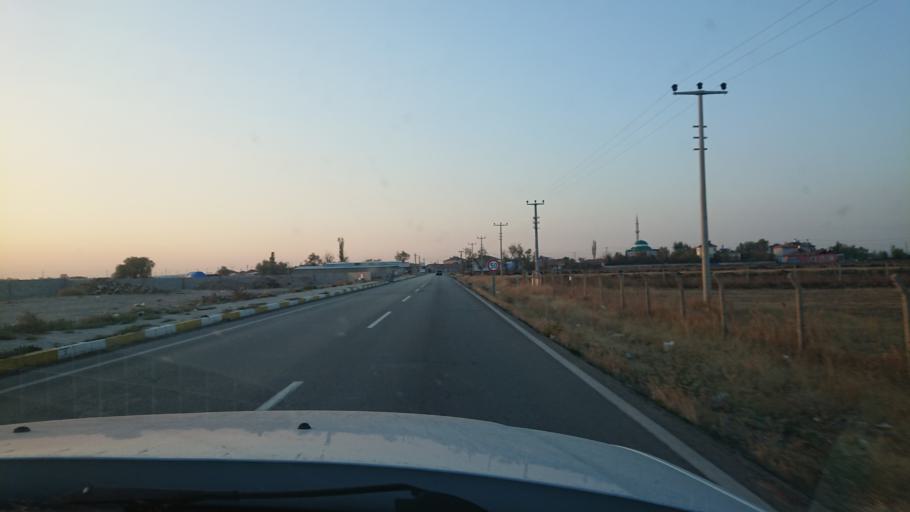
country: TR
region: Aksaray
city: Aksaray
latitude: 38.3157
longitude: 34.0560
